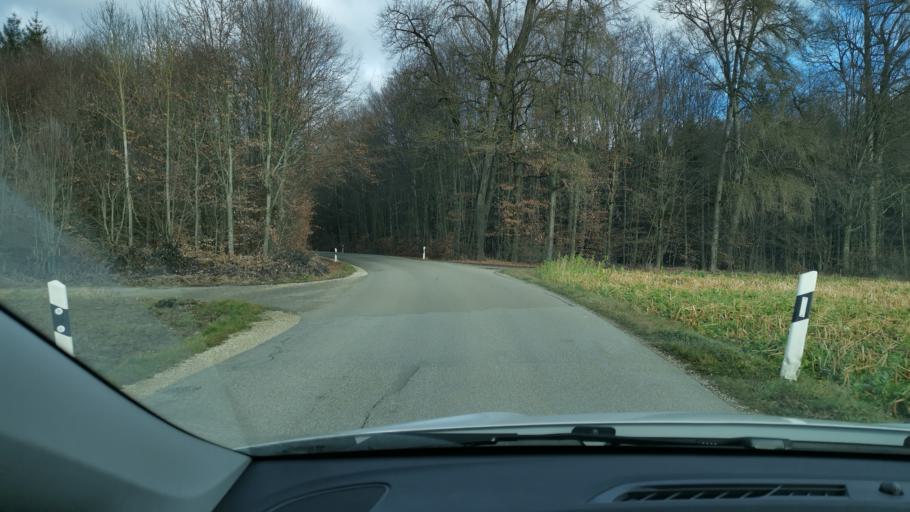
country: DE
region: Bavaria
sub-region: Swabia
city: Aindling
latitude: 48.5392
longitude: 10.9689
